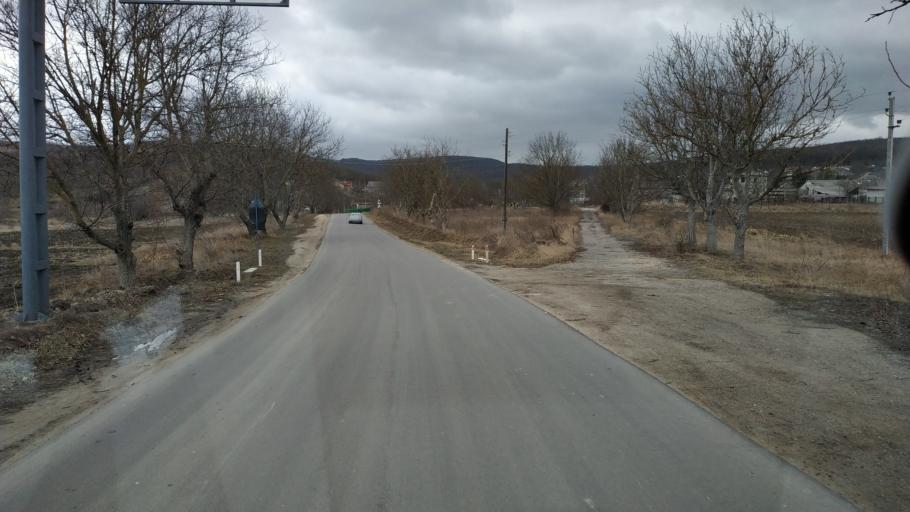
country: MD
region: Calarasi
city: Calarasi
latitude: 47.2484
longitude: 28.2867
